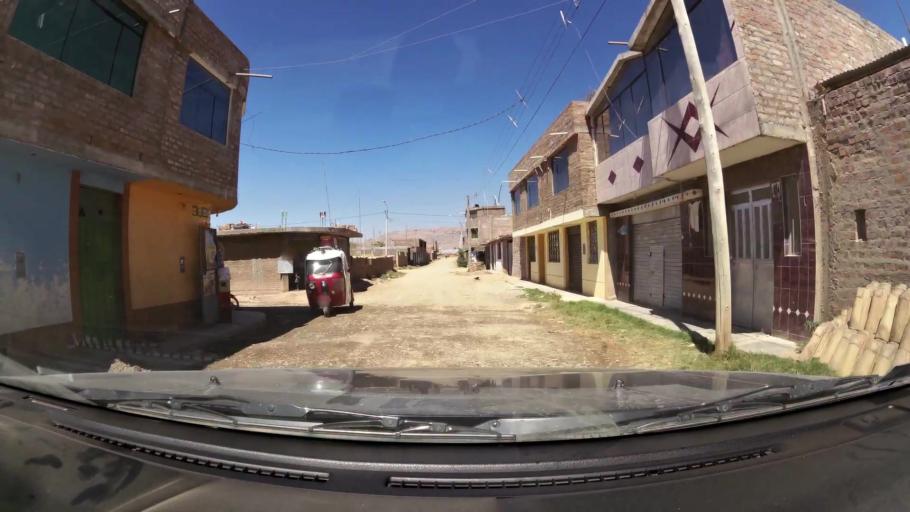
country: PE
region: Junin
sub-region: Provincia de Jauja
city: Jauja
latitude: -11.7743
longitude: -75.4898
